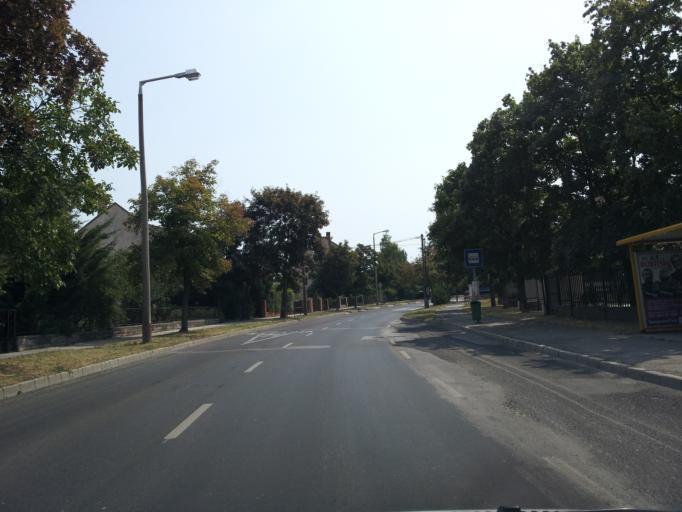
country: HU
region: Veszprem
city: Veszprem
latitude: 47.1019
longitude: 17.9246
